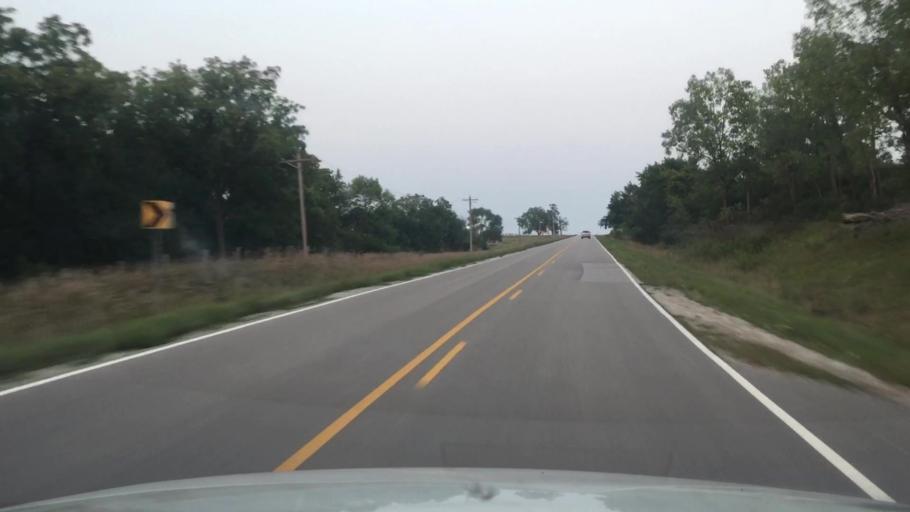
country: US
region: Iowa
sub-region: Warren County
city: Indianola
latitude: 41.1907
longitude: -93.5885
